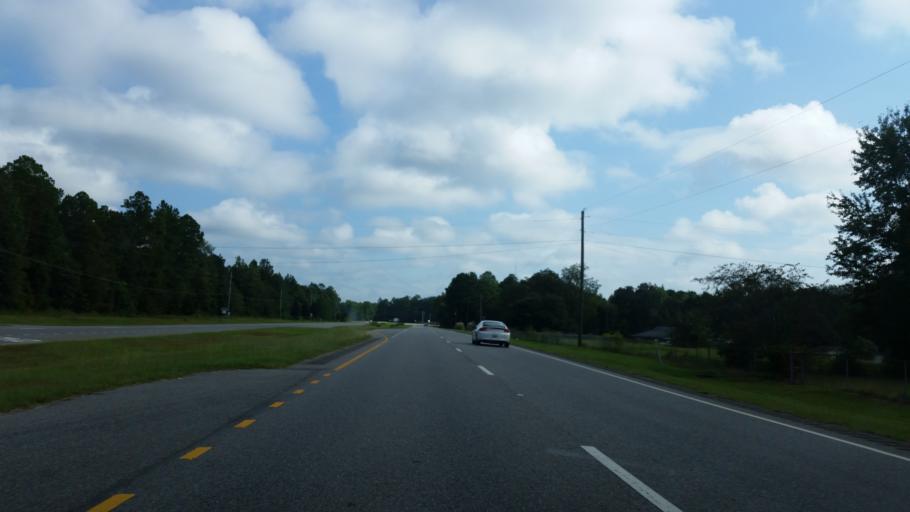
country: US
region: Alabama
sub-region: Baldwin County
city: Bay Minette
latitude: 30.9136
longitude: -87.7805
